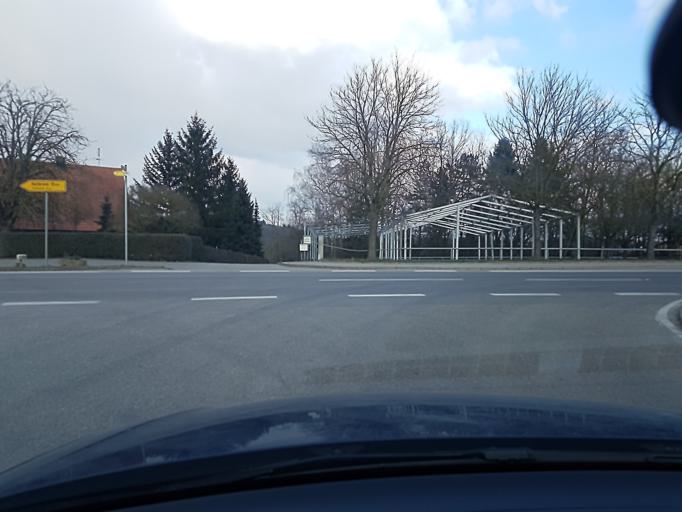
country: DE
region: Baden-Wuerttemberg
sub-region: Regierungsbezirk Stuttgart
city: Talheim
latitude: 49.0684
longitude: 9.1968
